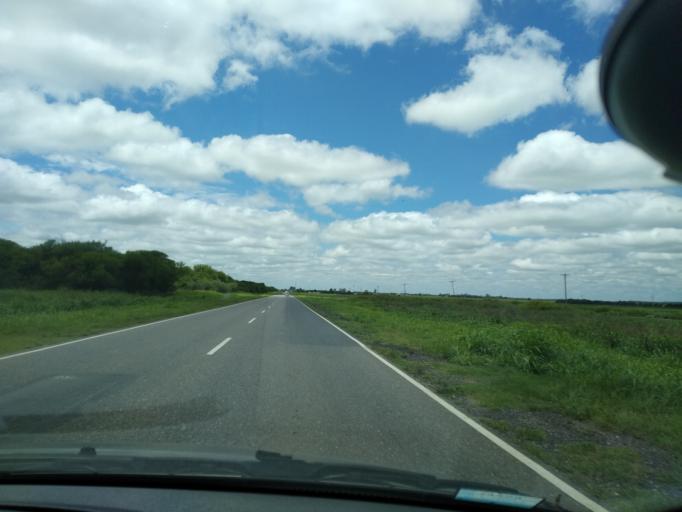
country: AR
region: Cordoba
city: Toledo
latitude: -31.6488
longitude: -64.1184
